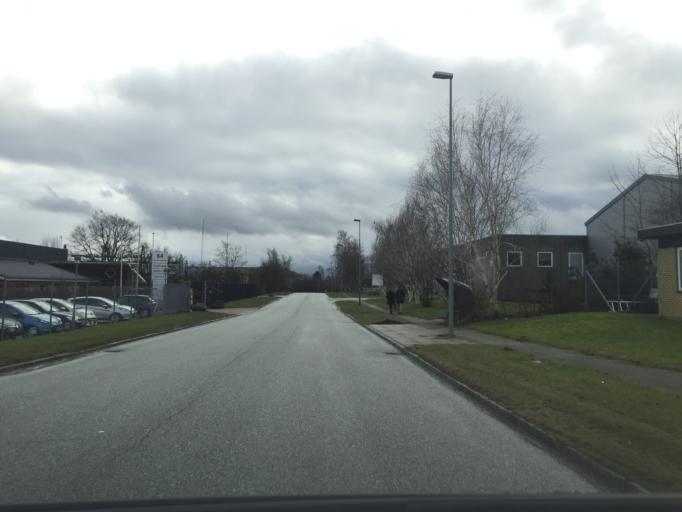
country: DK
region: Capital Region
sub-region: Fureso Kommune
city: Farum
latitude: 55.8209
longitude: 12.3628
